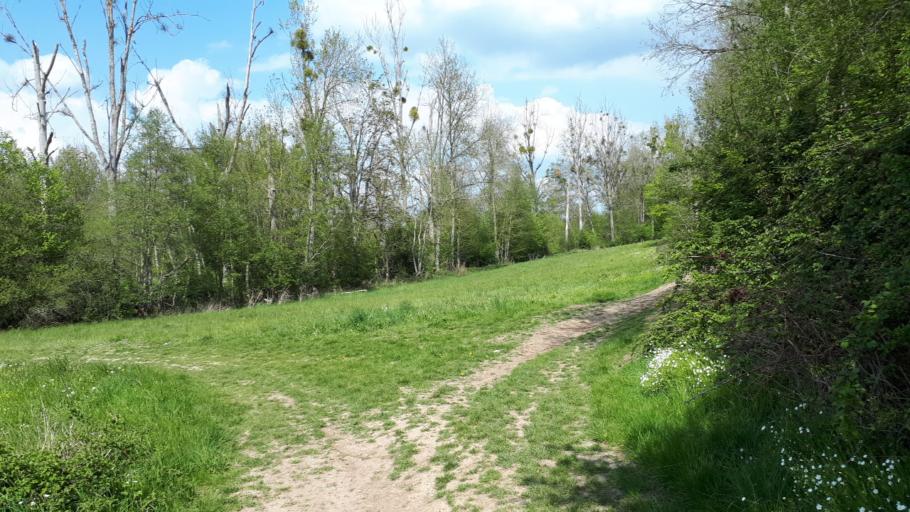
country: FR
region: Centre
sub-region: Departement du Loir-et-Cher
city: Villiers-sur-Loir
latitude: 47.8232
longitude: 0.9755
